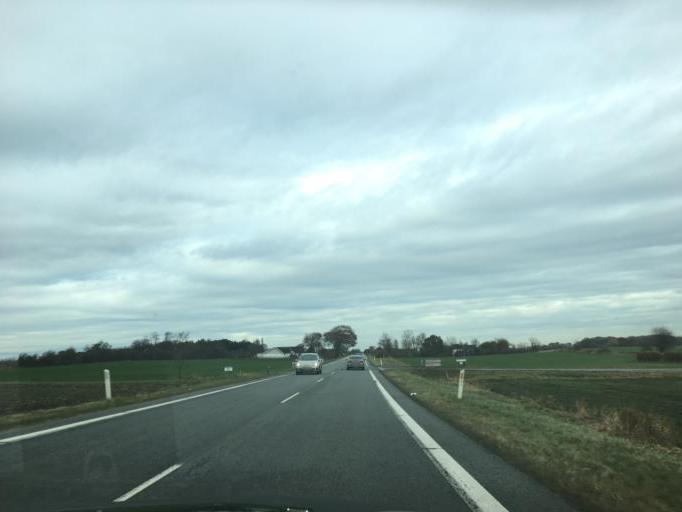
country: DK
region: South Denmark
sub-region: Vejle Kommune
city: Vejle
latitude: 55.6343
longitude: 9.4946
